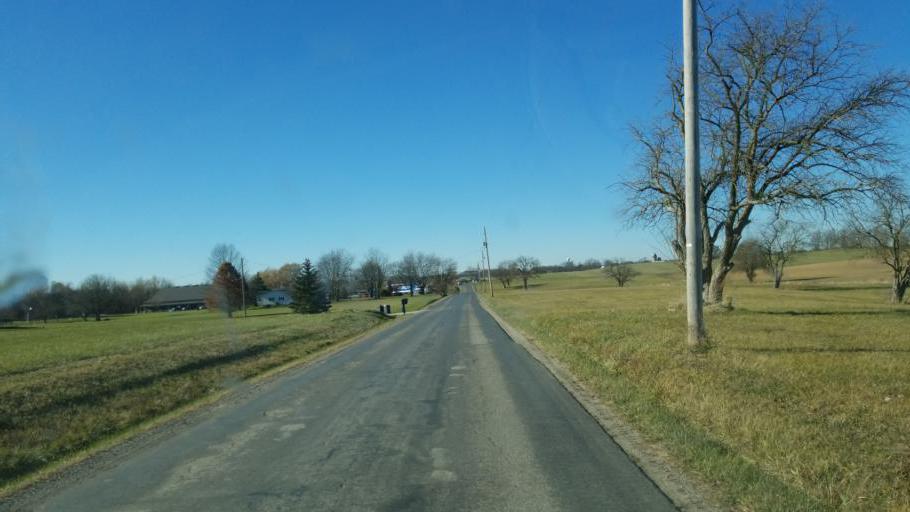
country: US
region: Ohio
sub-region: Huron County
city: Plymouth
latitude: 40.9601
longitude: -82.5808
